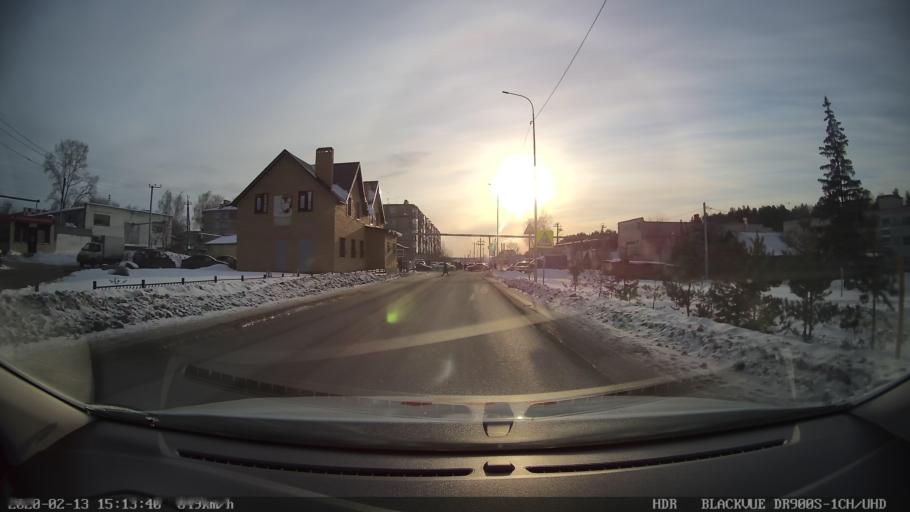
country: RU
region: Tatarstan
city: Vysokaya Gora
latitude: 55.9196
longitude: 49.3020
